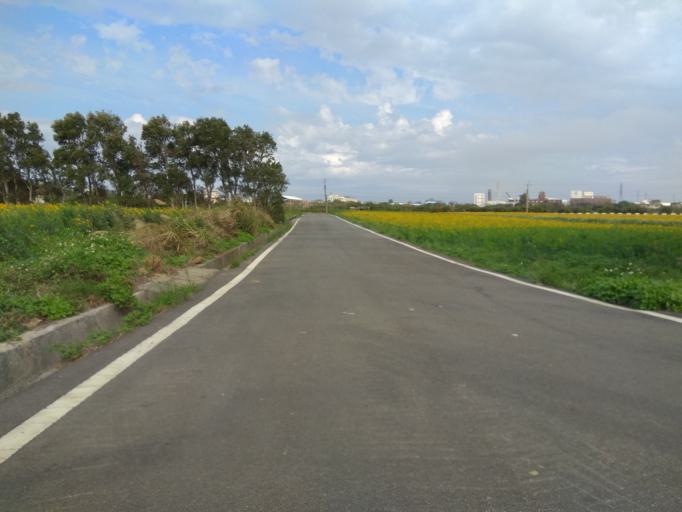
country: TW
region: Taiwan
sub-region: Hsinchu
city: Zhubei
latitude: 24.9789
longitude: 121.0324
